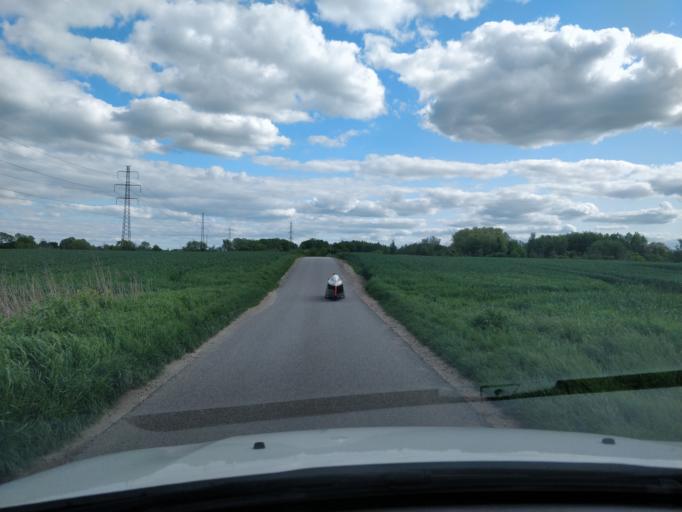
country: DK
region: Capital Region
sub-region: Hoje-Taastrup Kommune
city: Flong
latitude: 55.6835
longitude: 12.2194
